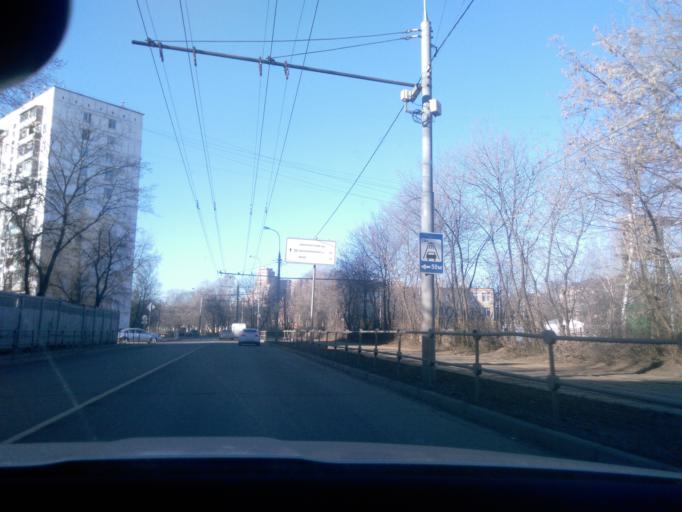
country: RU
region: Moskovskaya
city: Koptevo
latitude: 55.8126
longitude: 37.4929
